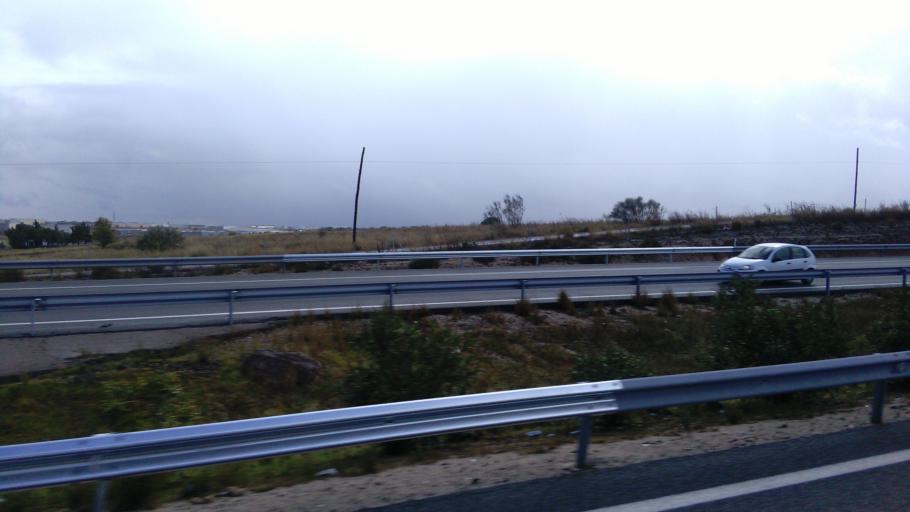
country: ES
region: Castille-La Mancha
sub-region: Province of Toledo
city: Valmojado
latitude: 40.2235
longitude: -4.0744
